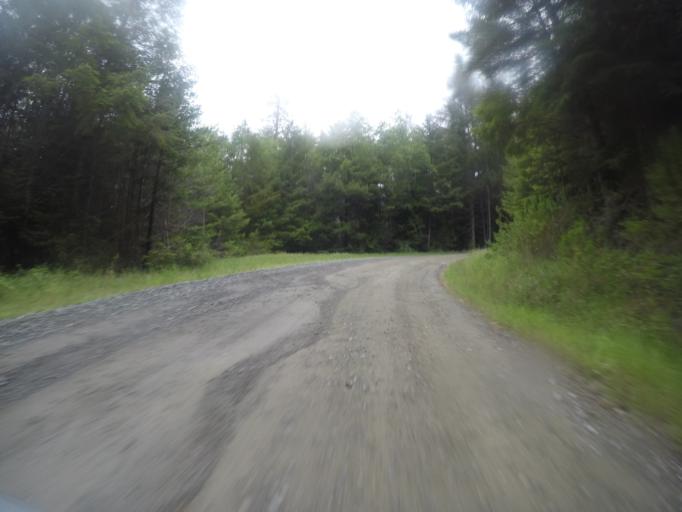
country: US
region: California
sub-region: Humboldt County
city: Westhaven-Moonstone
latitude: 41.2320
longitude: -123.9900
